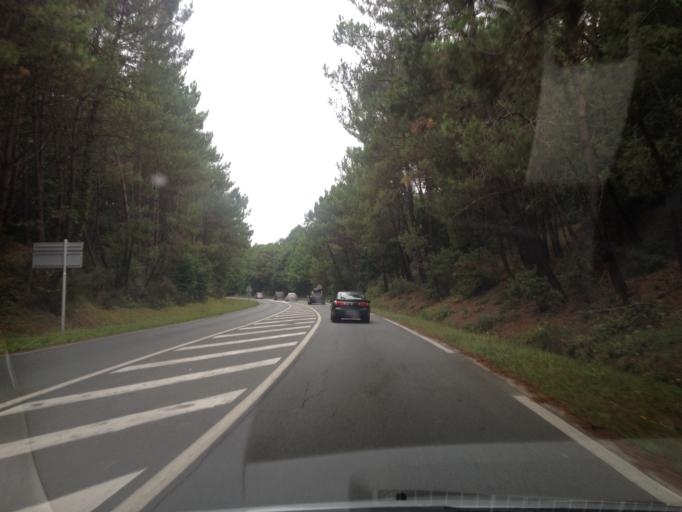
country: FR
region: Poitou-Charentes
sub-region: Departement de la Charente-Maritime
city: Vaux-sur-Mer
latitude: 45.6637
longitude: -1.0734
